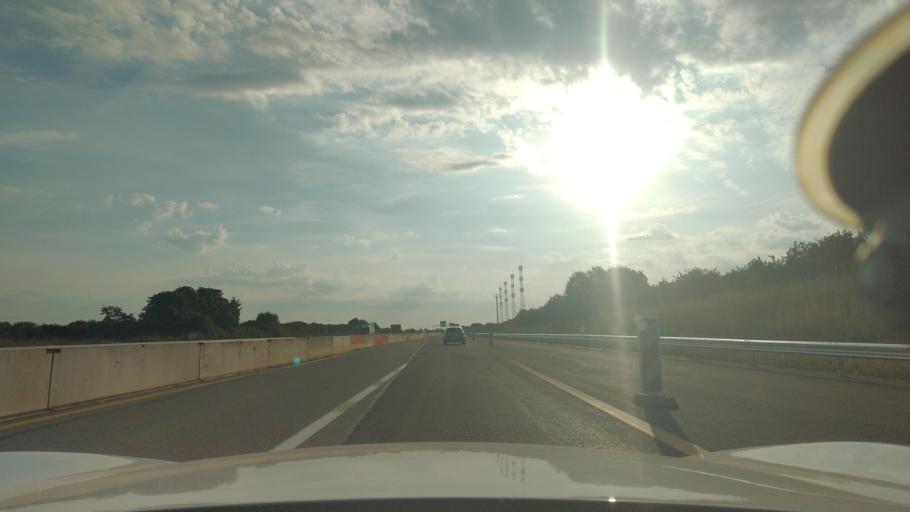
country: FR
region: Ile-de-France
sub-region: Departement du Val-d'Oise
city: Louvres
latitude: 49.0274
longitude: 2.5198
